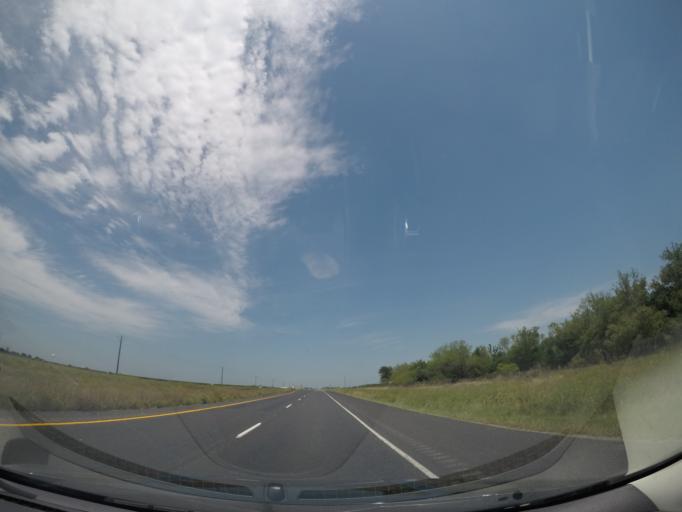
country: US
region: Texas
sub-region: Medina County
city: Hondo
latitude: 29.3362
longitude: -99.2126
